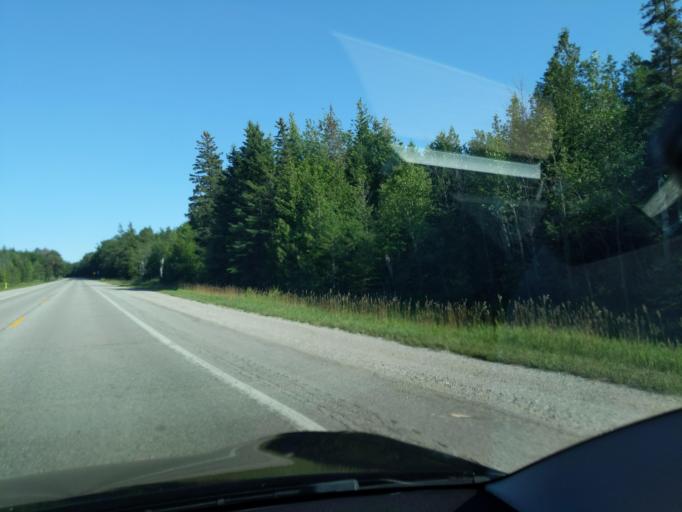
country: US
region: Michigan
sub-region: Mackinac County
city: Saint Ignace
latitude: 45.7530
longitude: -84.6920
